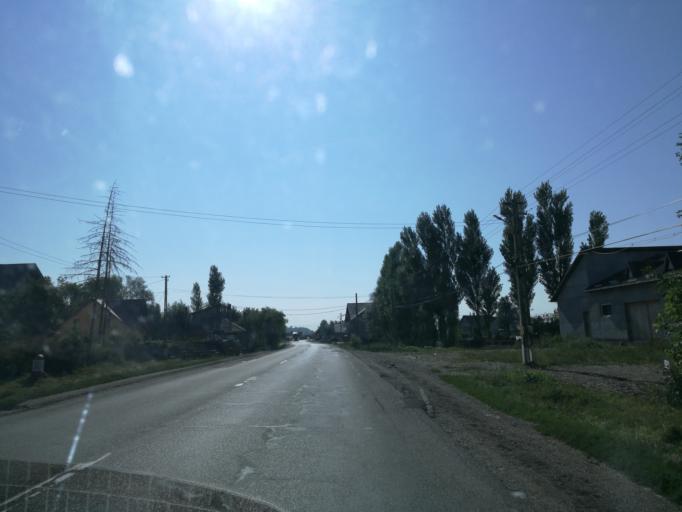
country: RO
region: Suceava
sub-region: Comuna Vadu Moldovei
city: Vadu Moldovei
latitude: 47.3707
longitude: 26.3804
